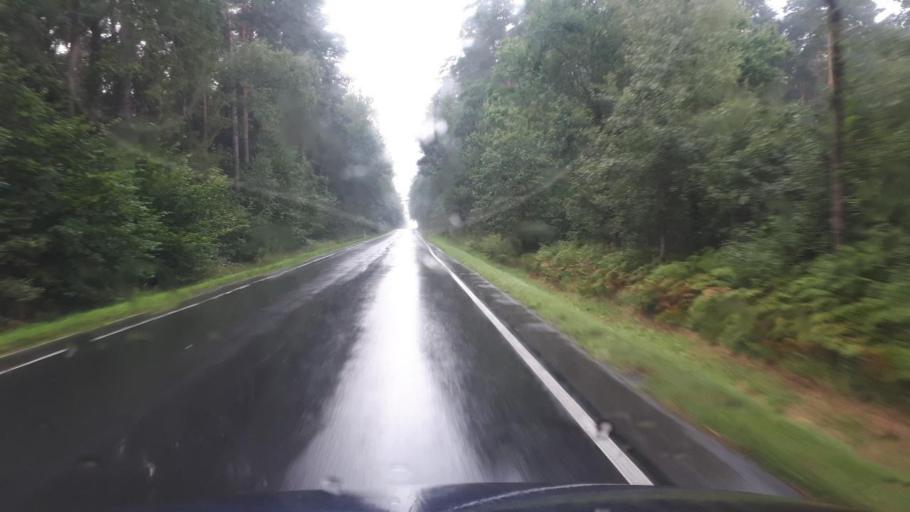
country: PL
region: Silesian Voivodeship
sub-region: Powiat gliwicki
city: Wielowies
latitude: 50.5291
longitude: 18.6636
